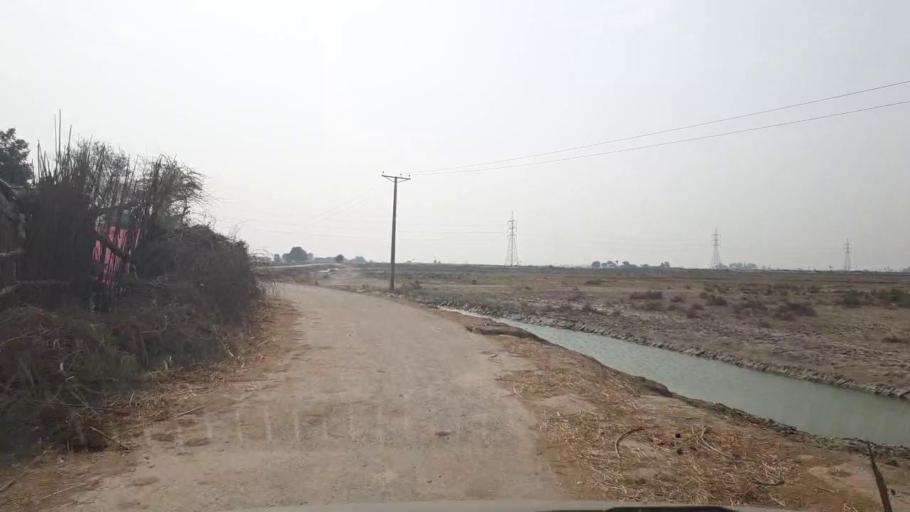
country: PK
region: Sindh
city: Tando Muhammad Khan
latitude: 25.1137
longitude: 68.3855
